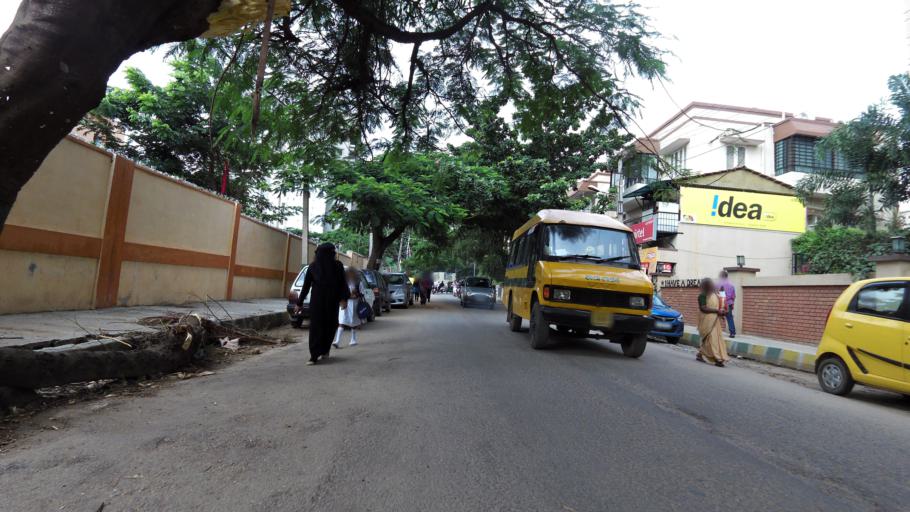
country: IN
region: Karnataka
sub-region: Bangalore Urban
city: Bangalore
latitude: 12.9998
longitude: 77.6291
